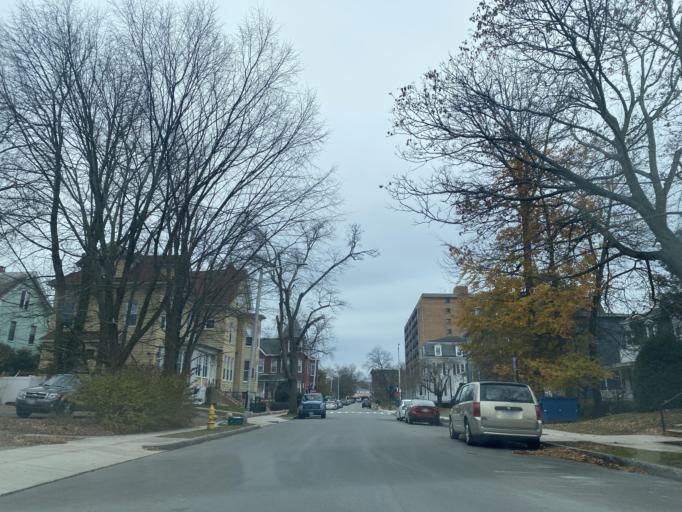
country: US
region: Massachusetts
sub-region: Worcester County
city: Worcester
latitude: 42.2665
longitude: -71.8119
